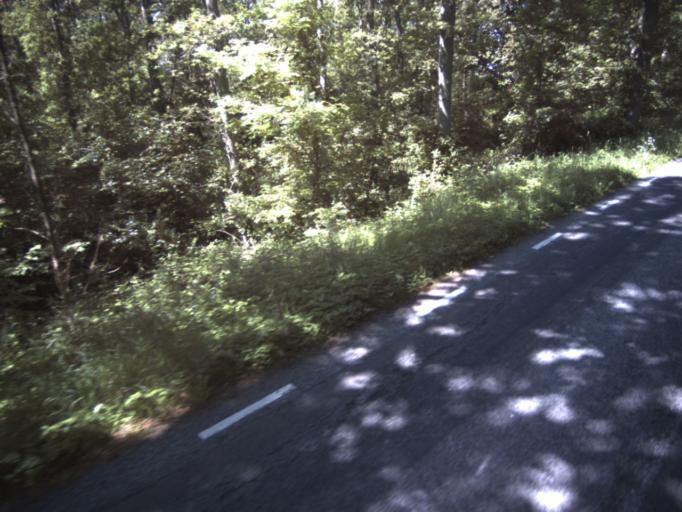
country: DK
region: Capital Region
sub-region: Helsingor Kommune
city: Hellebaek
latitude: 56.1132
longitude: 12.6175
